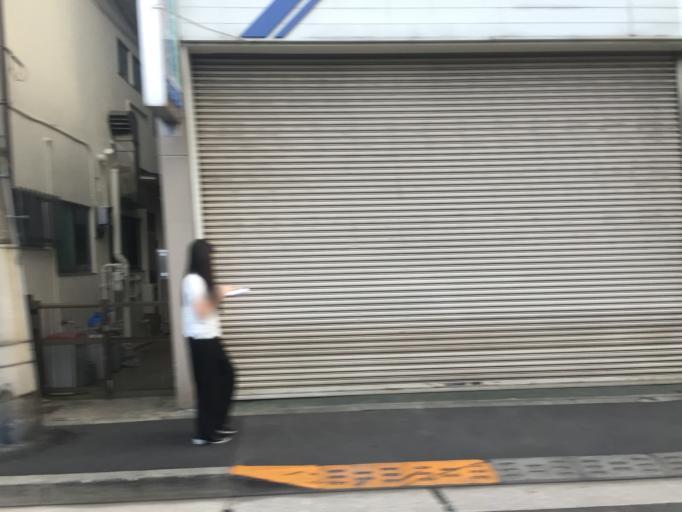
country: JP
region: Kanagawa
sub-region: Kawasaki-shi
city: Kawasaki
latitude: 35.5631
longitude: 139.6918
